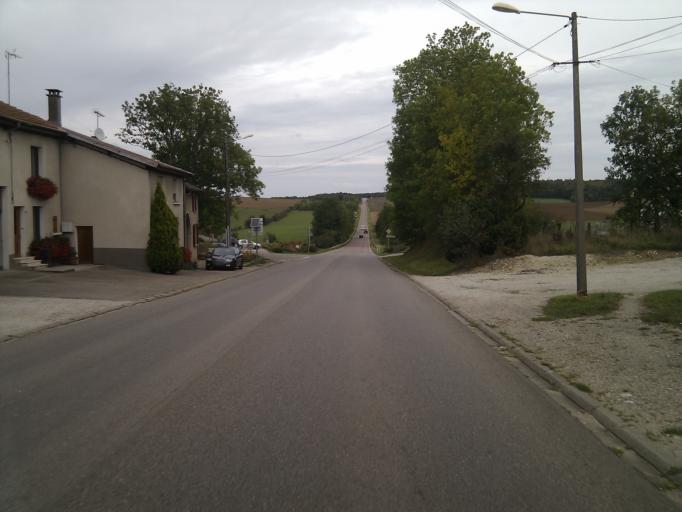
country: FR
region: Lorraine
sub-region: Departement de Meurthe-et-Moselle
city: Colombey-les-Belles
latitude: 48.4851
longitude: 5.8506
